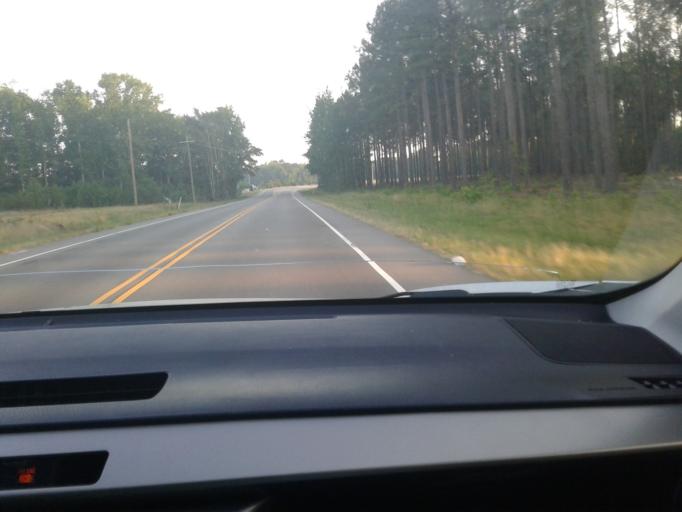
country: US
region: North Carolina
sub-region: Harnett County
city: Lillington
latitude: 35.4321
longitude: -78.8271
